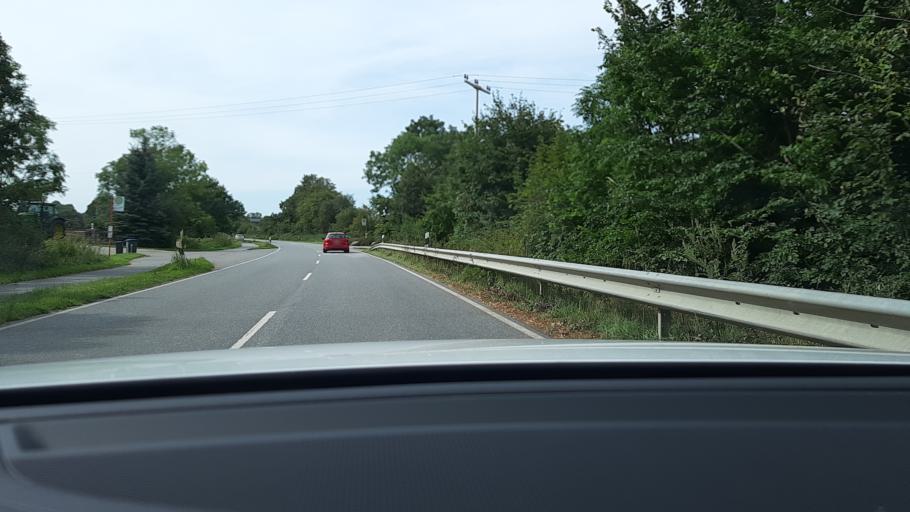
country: DE
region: Schleswig-Holstein
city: Monkhagen
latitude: 53.9115
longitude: 10.5370
